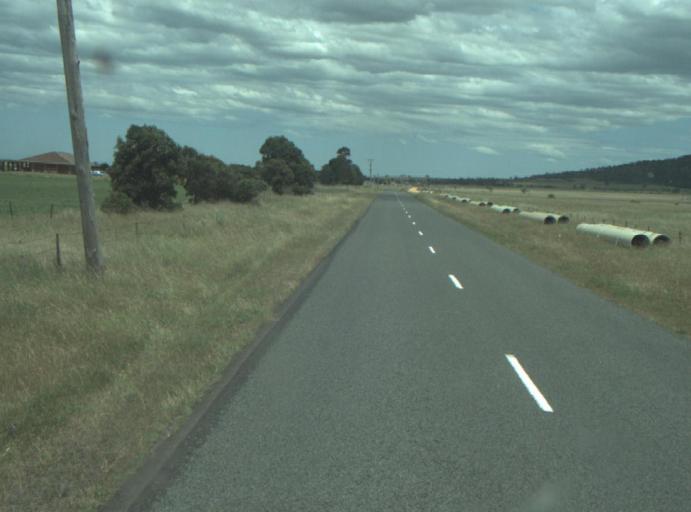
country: AU
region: Victoria
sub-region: Wyndham
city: Little River
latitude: -37.9064
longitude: 144.4635
